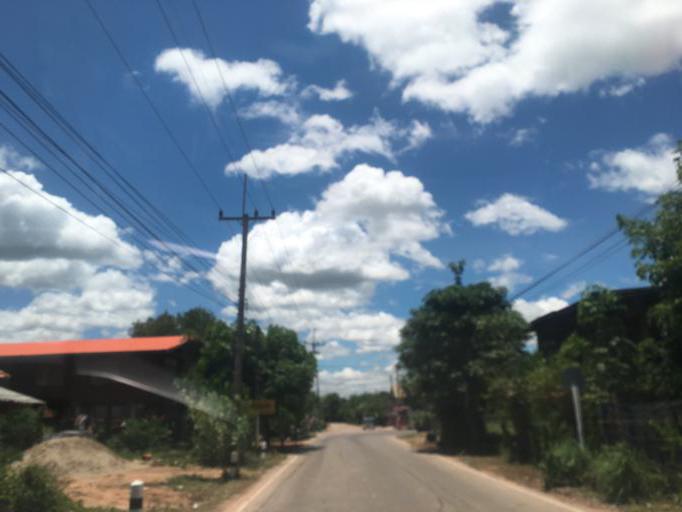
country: TH
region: Changwat Udon Thani
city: Nong Saeng
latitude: 17.2133
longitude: 102.7520
